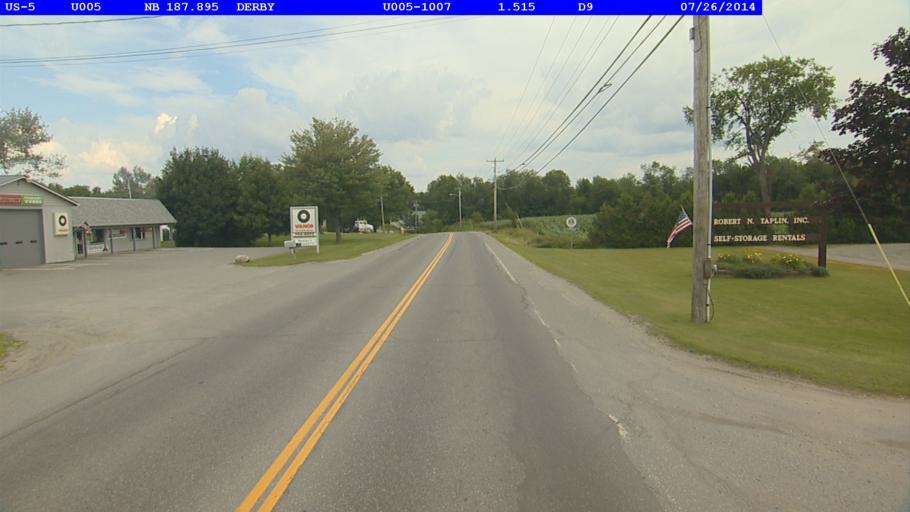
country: US
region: Vermont
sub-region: Orleans County
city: Newport
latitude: 44.9528
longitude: -72.1402
